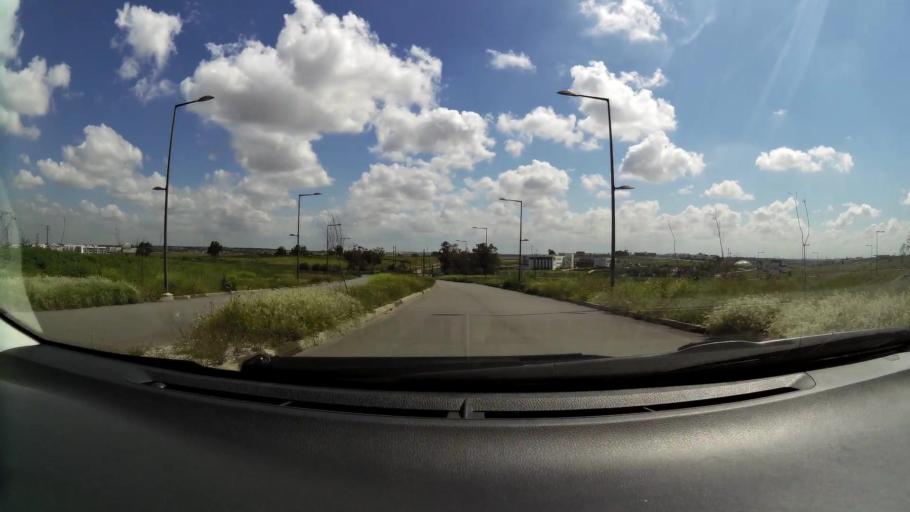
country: MA
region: Grand Casablanca
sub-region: Nouaceur
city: Bouskoura
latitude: 33.4997
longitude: -7.6085
